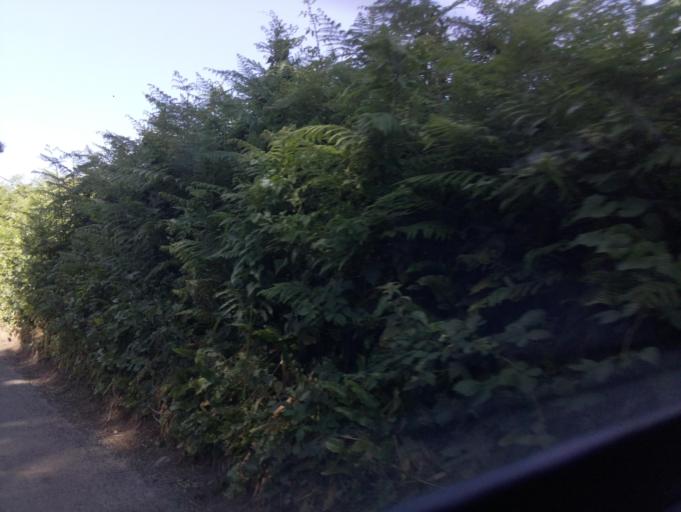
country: GB
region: England
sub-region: Devon
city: Marldon
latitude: 50.4109
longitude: -3.6155
